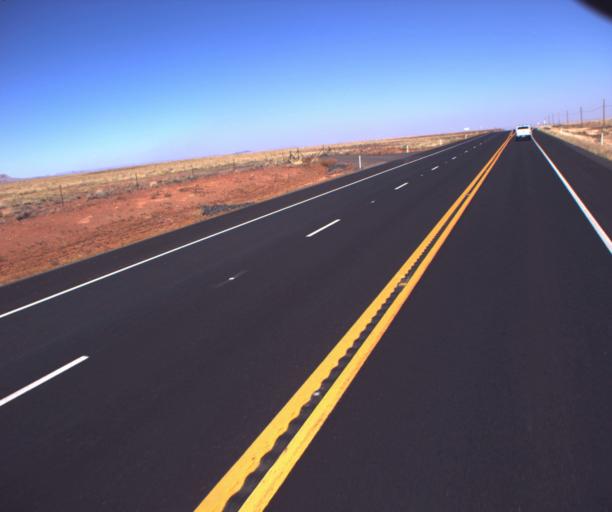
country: US
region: Arizona
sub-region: Coconino County
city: Tuba City
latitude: 35.7130
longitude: -111.4903
